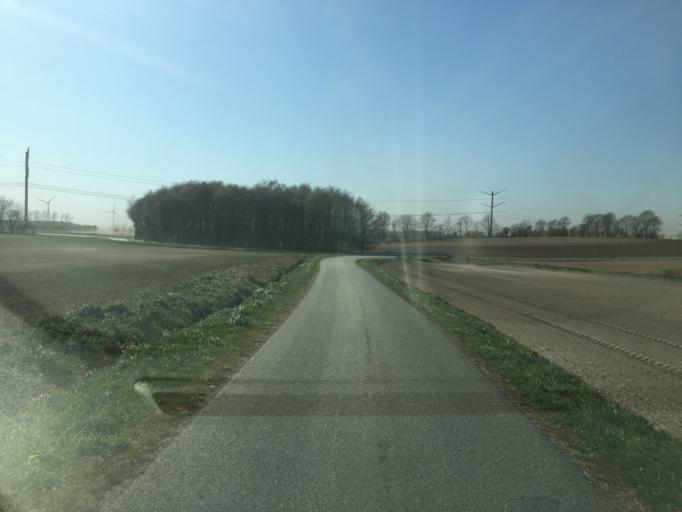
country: DK
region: South Denmark
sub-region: Aabenraa Kommune
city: Rodekro
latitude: 55.1082
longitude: 9.2212
